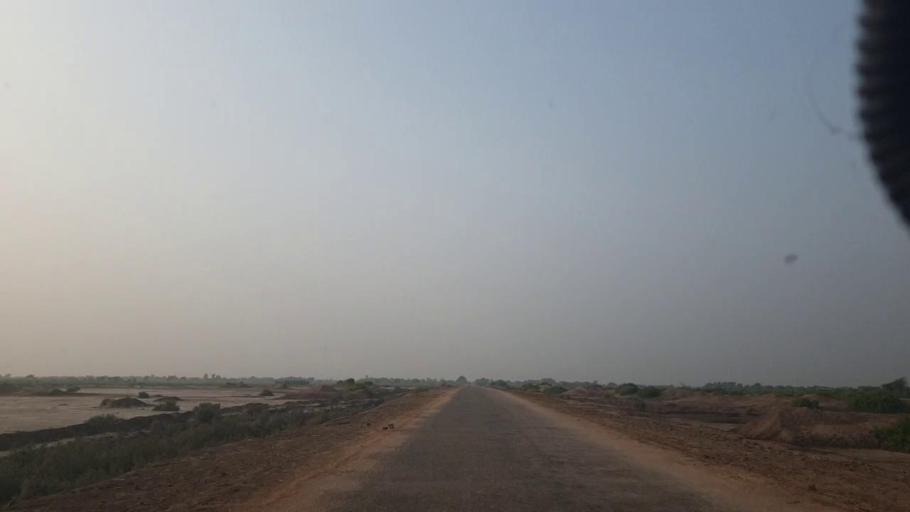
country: PK
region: Sindh
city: Bulri
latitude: 24.8562
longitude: 68.4015
